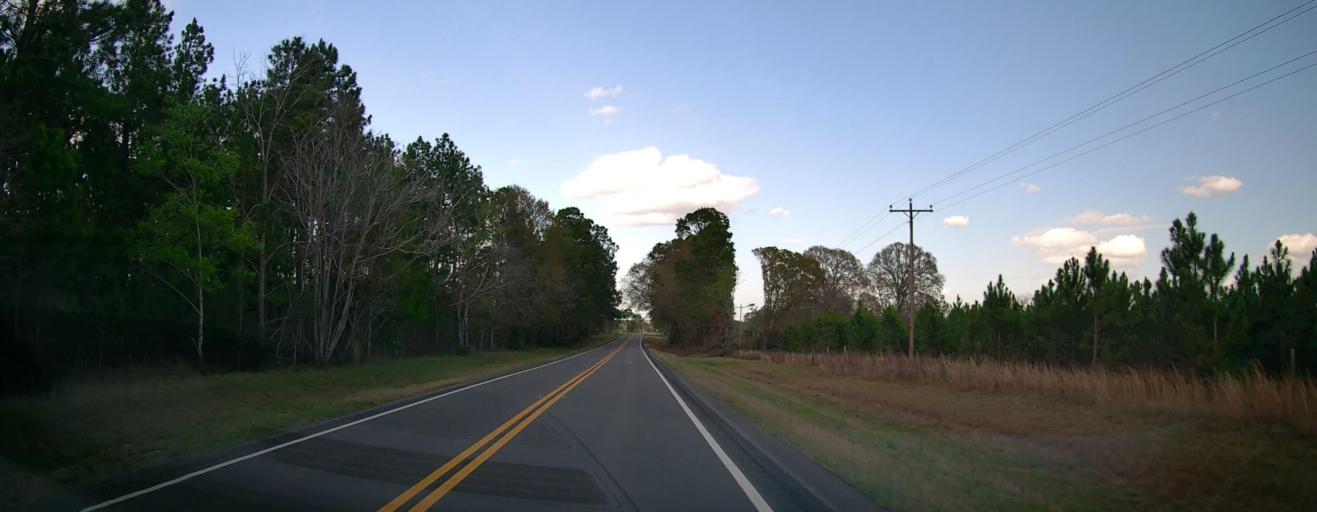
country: US
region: Georgia
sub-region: Wheeler County
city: Alamo
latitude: 32.1156
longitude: -82.7968
